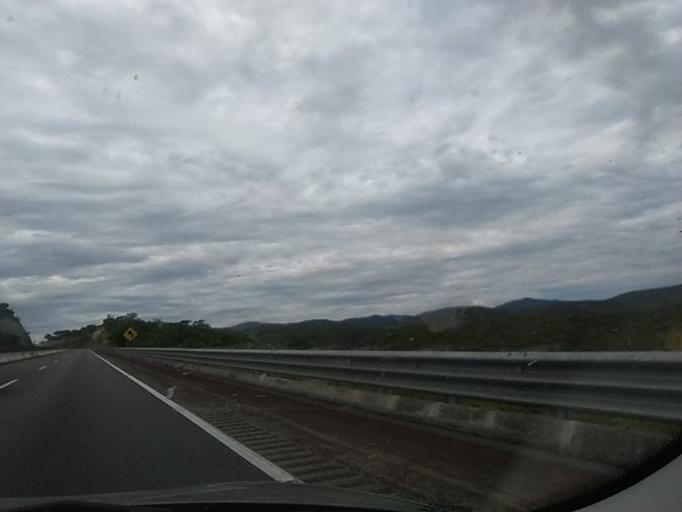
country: MX
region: Guerrero
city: Copalillo
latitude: 18.0936
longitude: -99.2187
